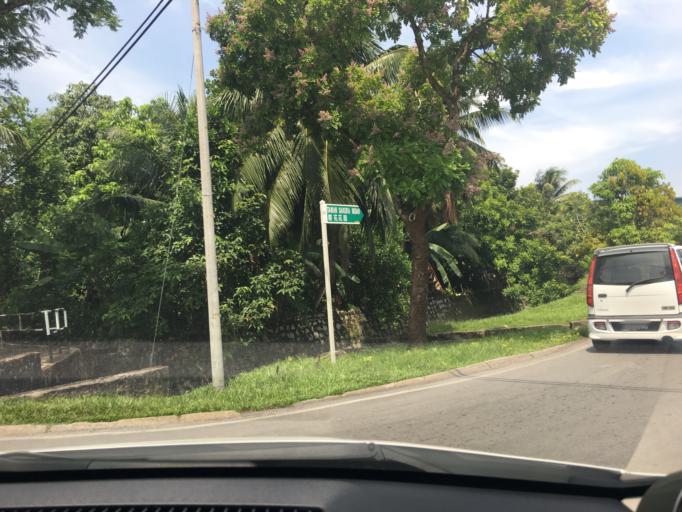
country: MY
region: Sarawak
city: Kuching
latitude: 1.5075
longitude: 110.3022
